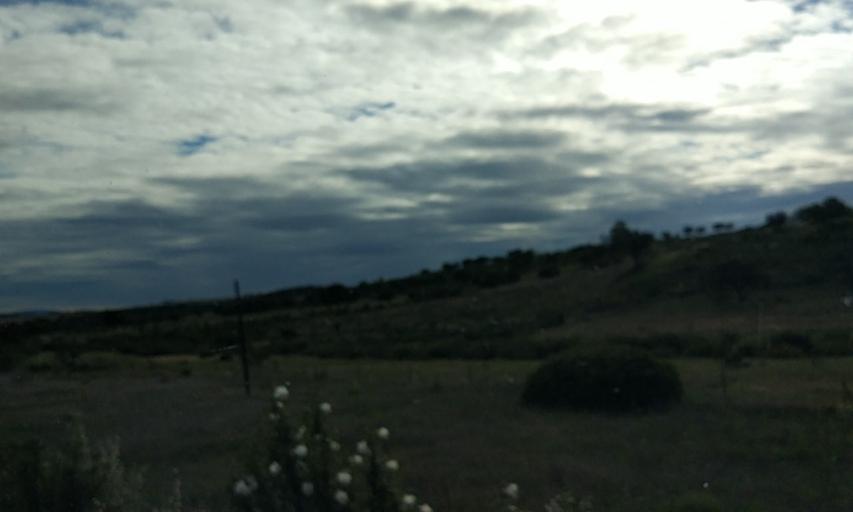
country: ES
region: Extremadura
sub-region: Provincia de Caceres
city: Perales del Puerto
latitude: 40.1156
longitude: -6.6702
